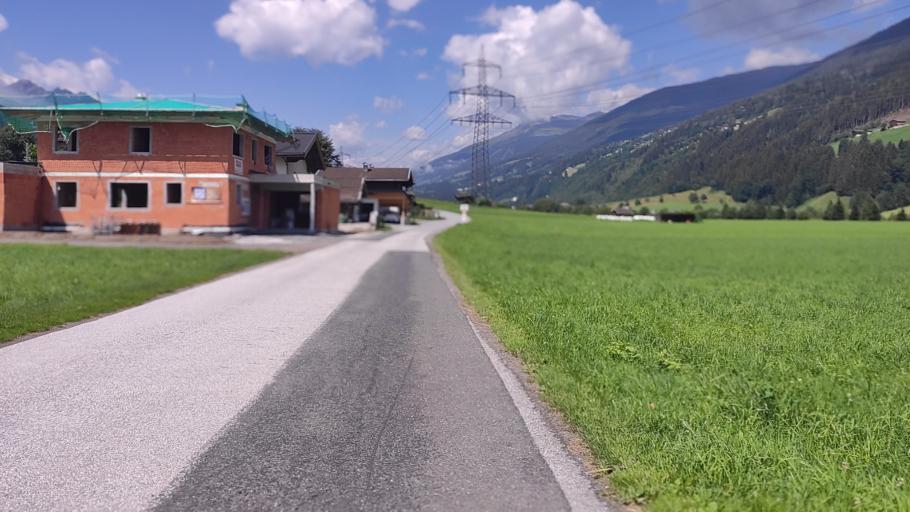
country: AT
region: Salzburg
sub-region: Politischer Bezirk Zell am See
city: Neukirchen am Grossvenediger
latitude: 47.2524
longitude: 12.3123
